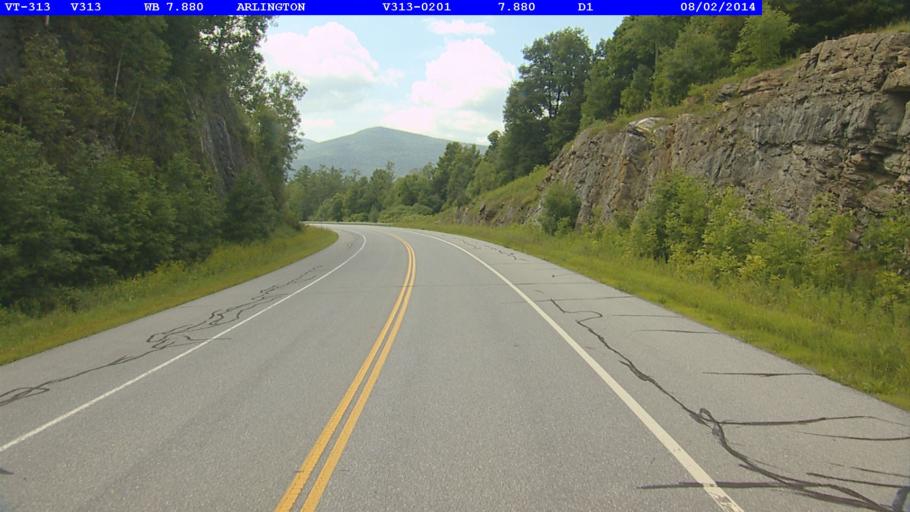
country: US
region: Vermont
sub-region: Bennington County
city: Arlington
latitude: 43.0535
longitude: -73.1396
